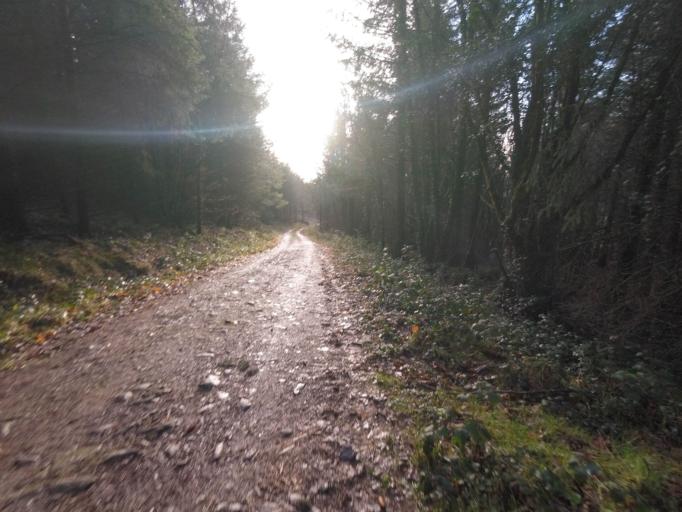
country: IE
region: Munster
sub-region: Waterford
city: Portlaw
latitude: 52.3144
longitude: -7.3477
